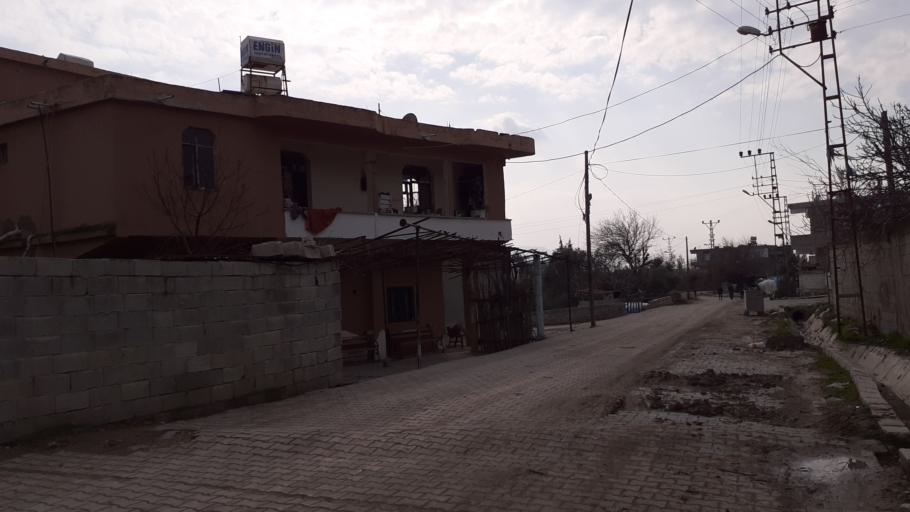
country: TR
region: Hatay
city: Kastal
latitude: 36.2634
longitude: 36.2447
